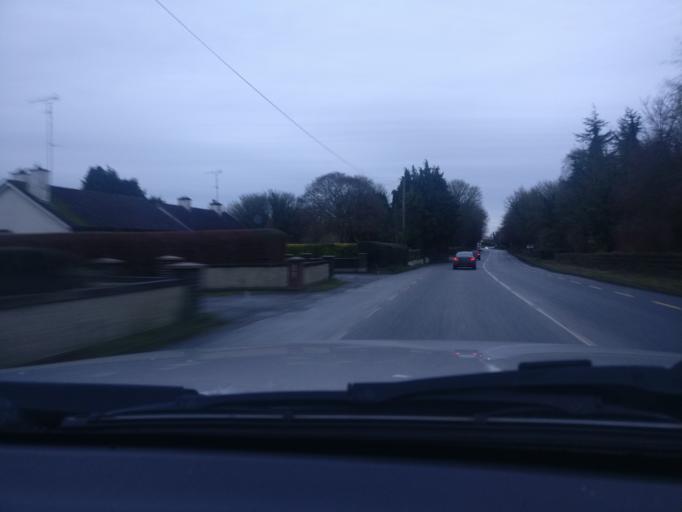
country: IE
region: Leinster
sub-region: An Mhi
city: Navan
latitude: 53.6575
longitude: -6.7108
